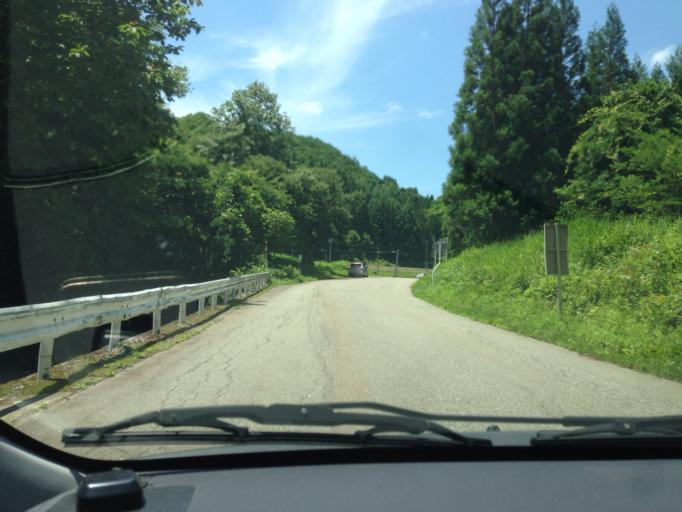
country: JP
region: Tochigi
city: Kuroiso
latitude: 37.2543
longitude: 139.7707
